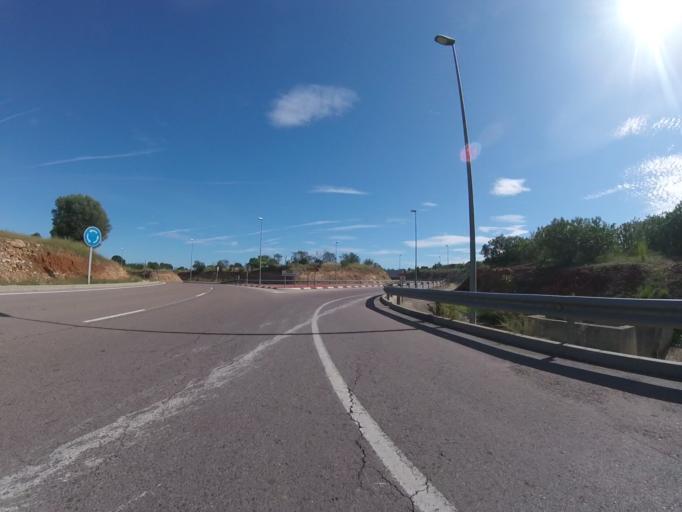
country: ES
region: Valencia
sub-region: Provincia de Castello
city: Peniscola
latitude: 40.3937
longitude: 0.3575
